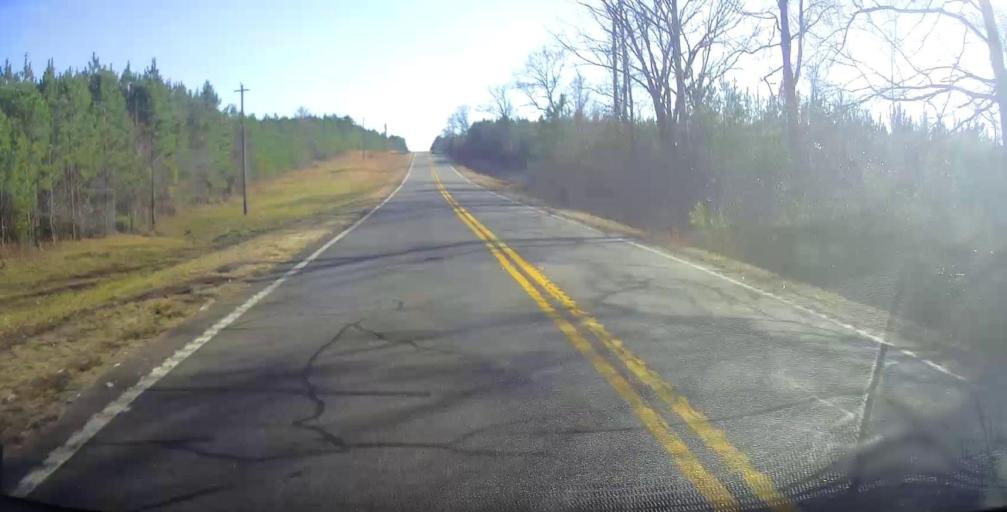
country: US
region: Georgia
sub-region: Talbot County
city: Talbotton
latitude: 32.7268
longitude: -84.5555
